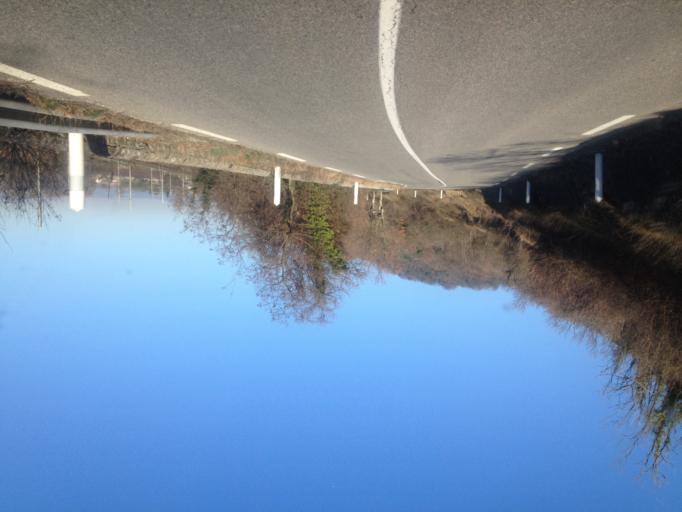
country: FR
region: Rhone-Alpes
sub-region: Departement de la Drome
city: Saulce-sur-Rhone
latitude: 44.7035
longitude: 4.7654
